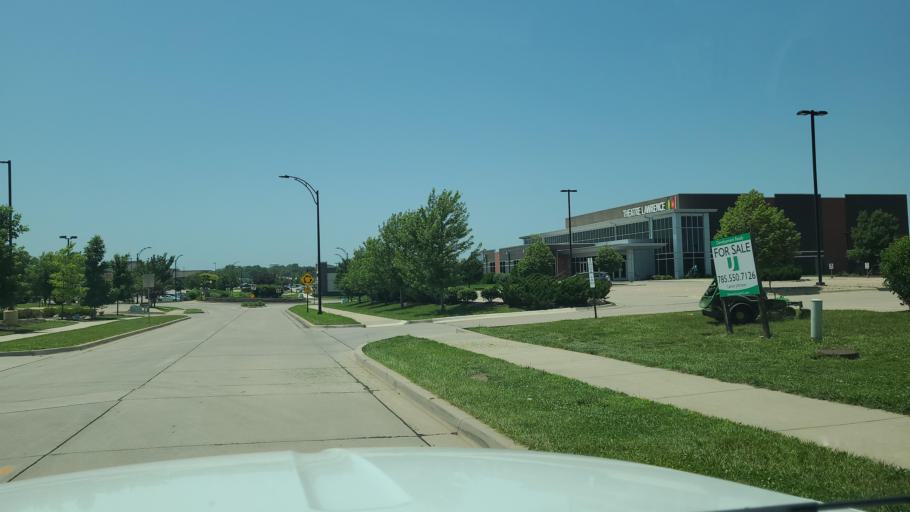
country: US
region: Kansas
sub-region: Douglas County
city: Lawrence
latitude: 38.9721
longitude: -95.3015
